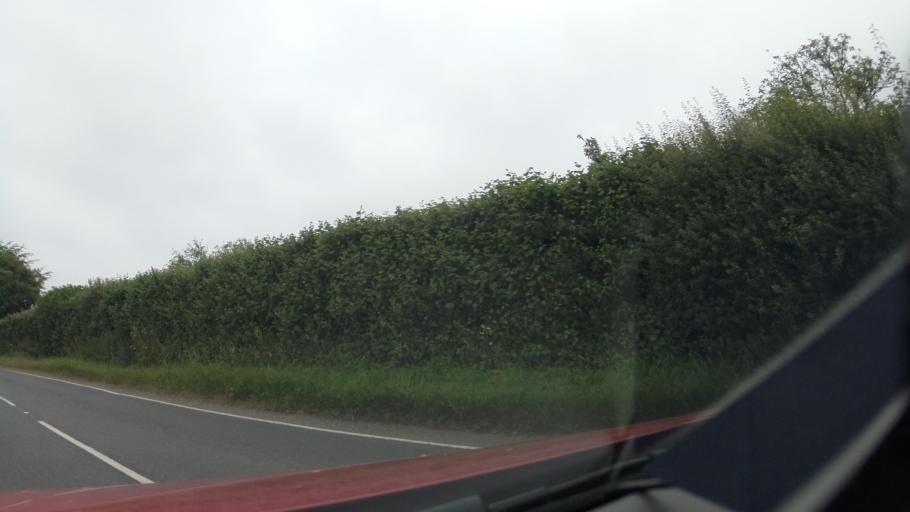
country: GB
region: England
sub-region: Dorset
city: Beaminster
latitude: 50.7682
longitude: -2.7334
